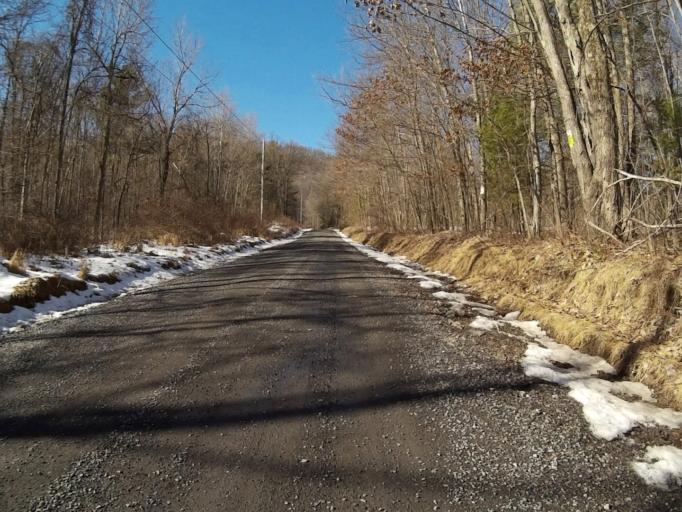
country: US
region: Pennsylvania
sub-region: Centre County
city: Stormstown
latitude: 40.8541
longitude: -78.0518
